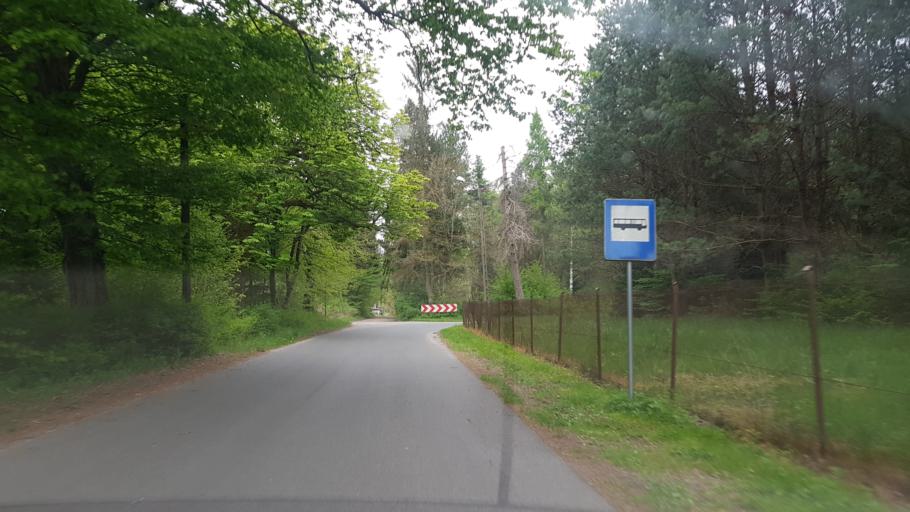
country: PL
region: West Pomeranian Voivodeship
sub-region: Powiat koszalinski
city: Polanow
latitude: 54.2023
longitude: 16.5046
